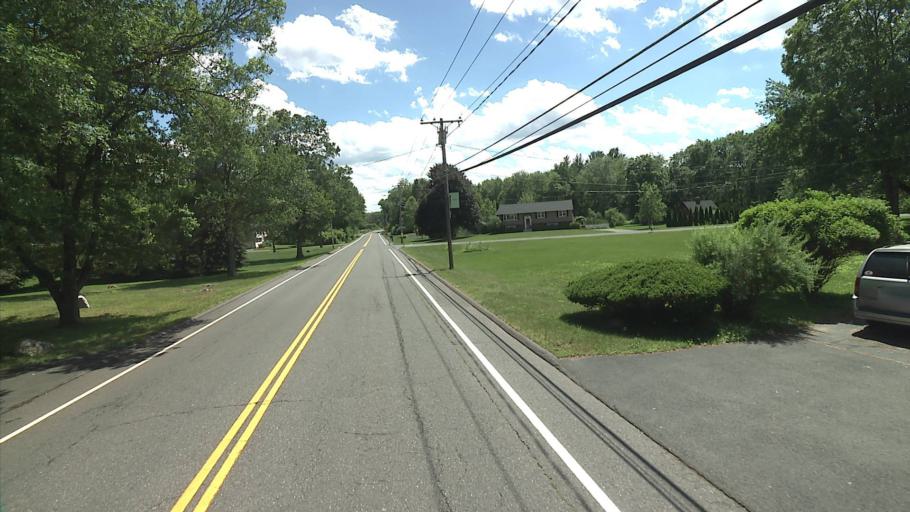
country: US
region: Connecticut
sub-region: Tolland County
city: Somers
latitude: 42.0145
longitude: -72.4829
